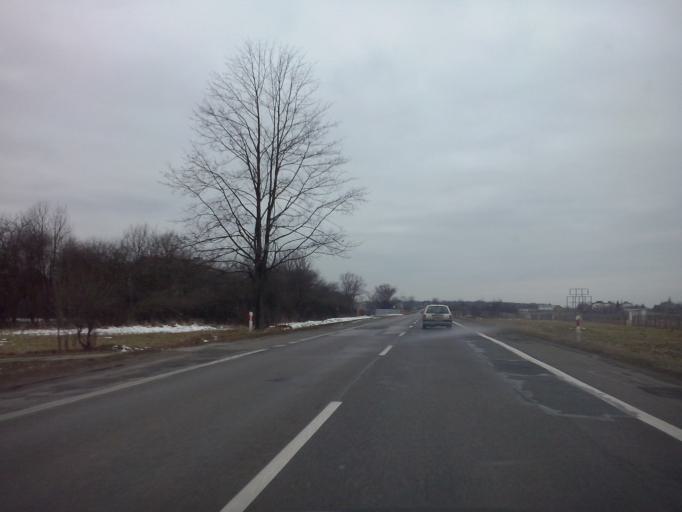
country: PL
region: Subcarpathian Voivodeship
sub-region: Powiat nizanski
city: Raclawice
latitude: 50.5180
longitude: 22.1712
